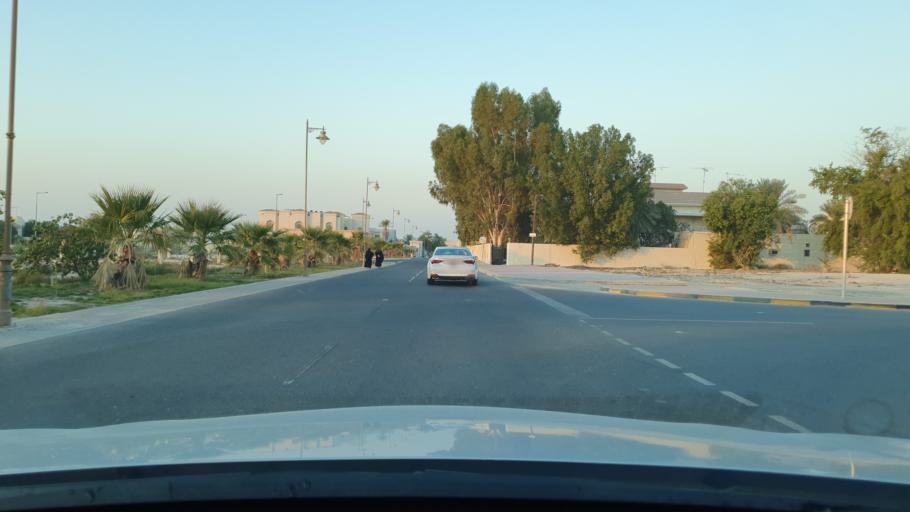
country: BH
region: Northern
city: Ar Rifa'
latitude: 26.1367
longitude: 50.5323
